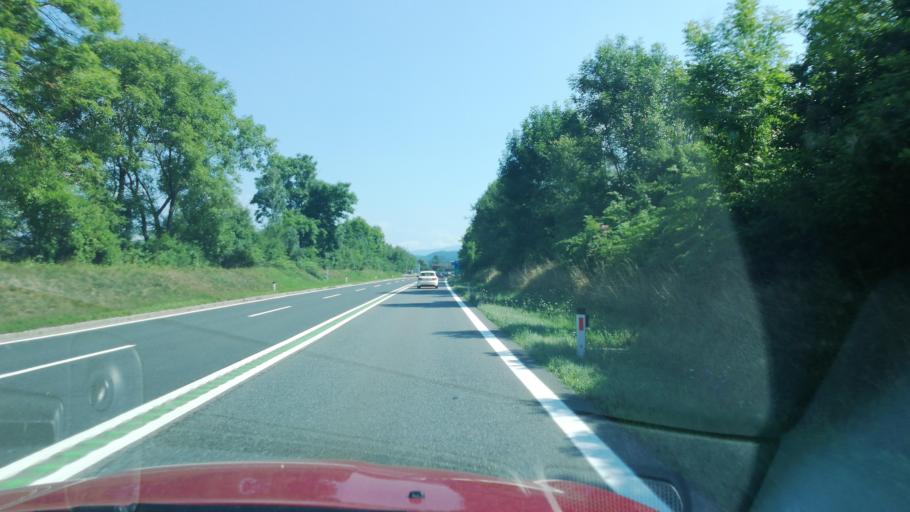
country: AT
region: Carinthia
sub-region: Politischer Bezirk Klagenfurt Land
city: Maria Saal
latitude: 46.6773
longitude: 14.3292
